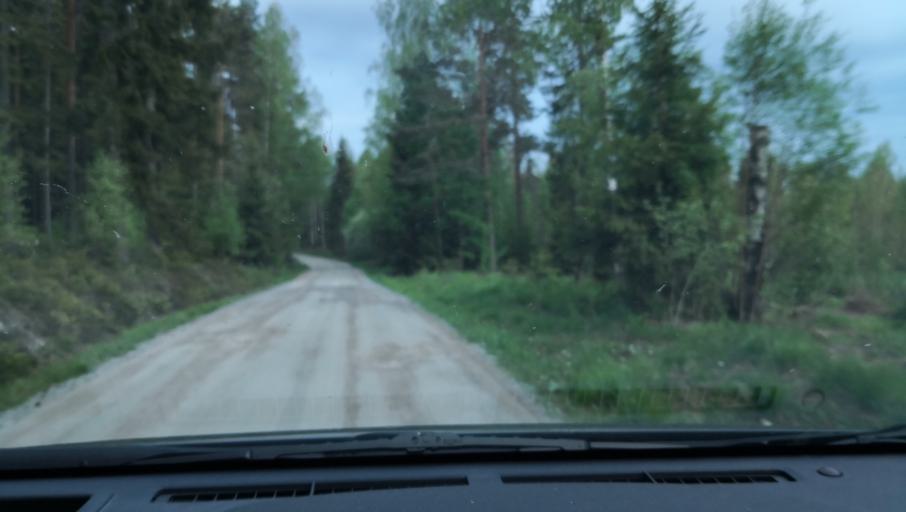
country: SE
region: Vaestmanland
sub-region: Skinnskattebergs Kommun
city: Skinnskatteberg
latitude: 59.7360
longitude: 15.4707
